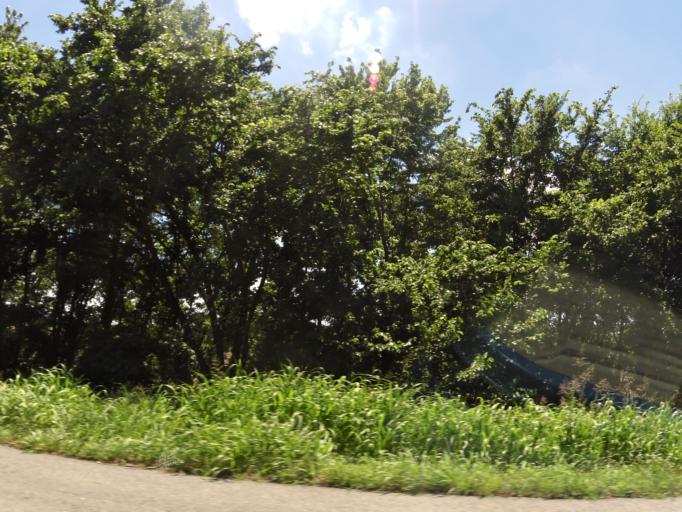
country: US
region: Missouri
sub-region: Pemiscot County
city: Caruthersville
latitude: 36.1306
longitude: -89.6232
